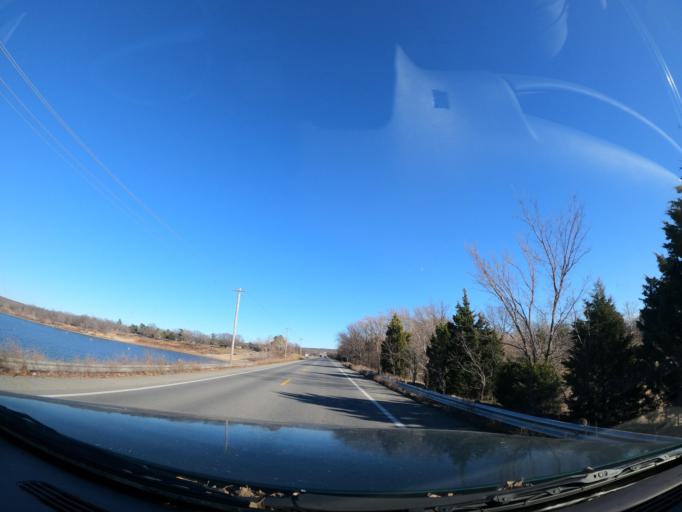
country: US
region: Oklahoma
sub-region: Pittsburg County
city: Longtown
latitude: 35.2392
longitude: -95.4965
